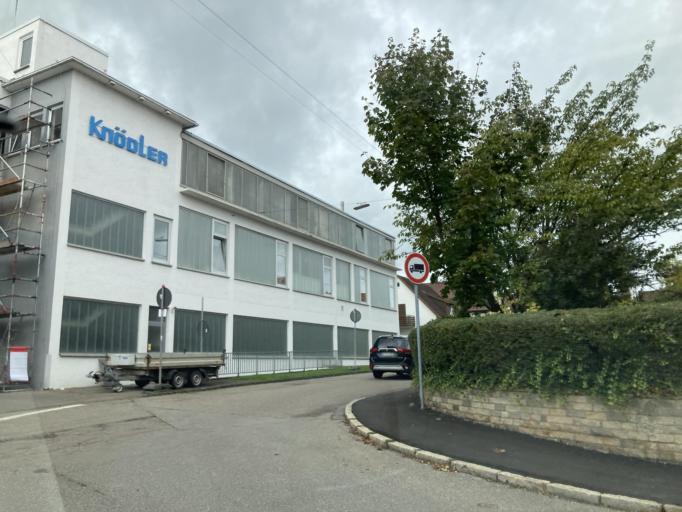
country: DE
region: Baden-Wuerttemberg
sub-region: Regierungsbezirk Stuttgart
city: Ostfildern
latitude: 48.7261
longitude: 9.2527
